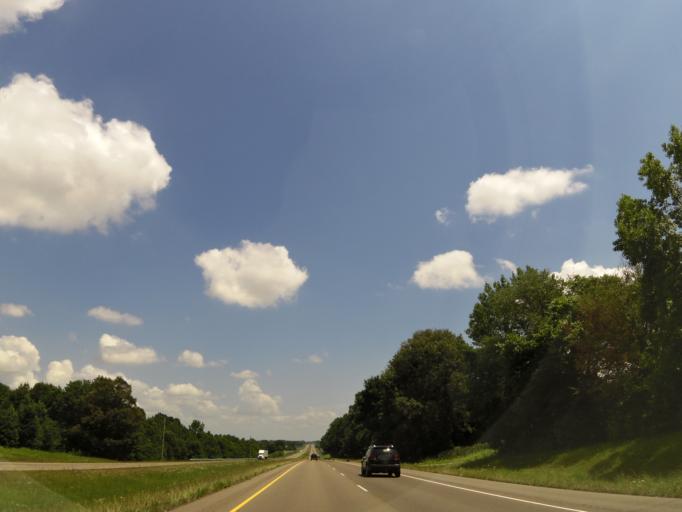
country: US
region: Tennessee
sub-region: Lauderdale County
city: Halls
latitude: 35.9083
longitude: -89.2599
